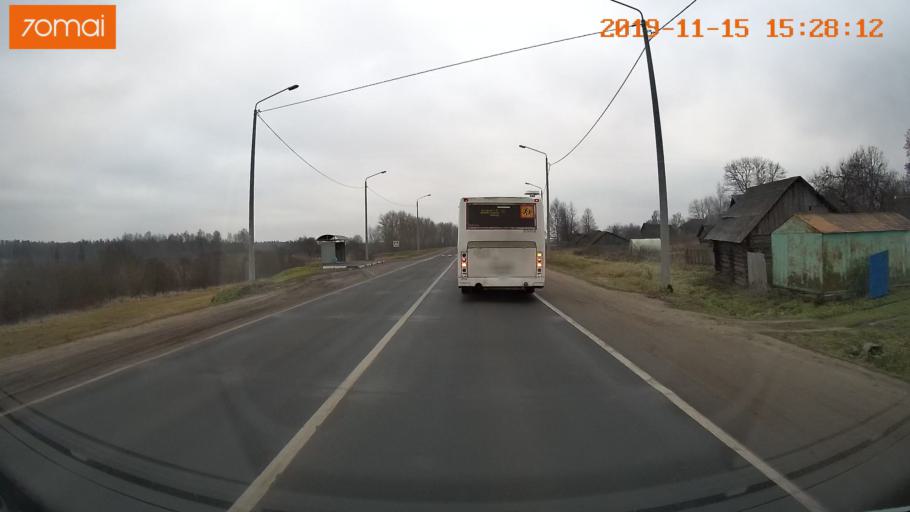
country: RU
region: Jaroslavl
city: Danilov
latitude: 58.1342
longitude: 40.1369
